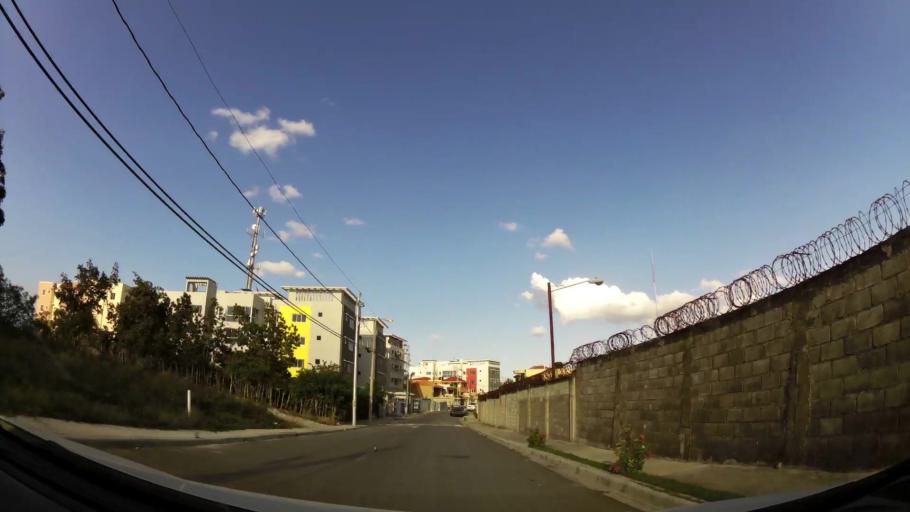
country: DO
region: Nacional
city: Ensanche Luperon
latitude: 18.5479
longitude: -69.9086
